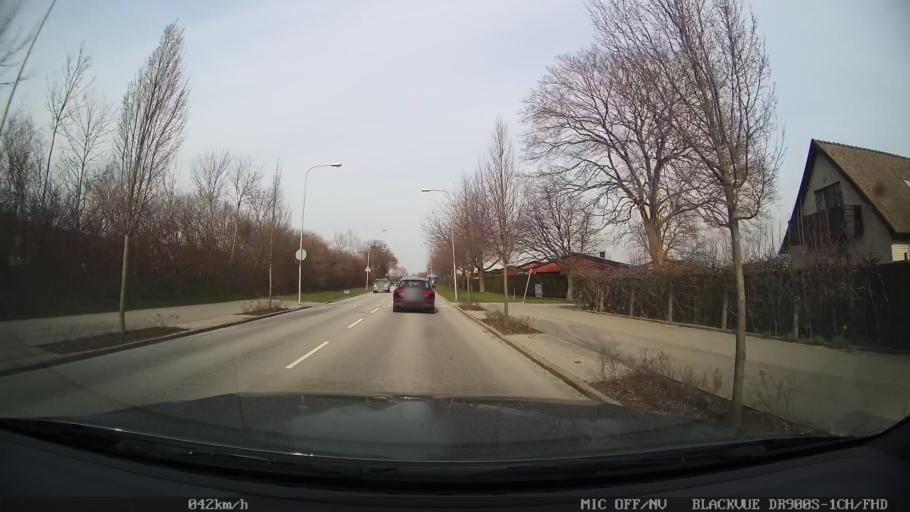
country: SE
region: Skane
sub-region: Ystads Kommun
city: Ystad
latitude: 55.4415
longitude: 13.8315
